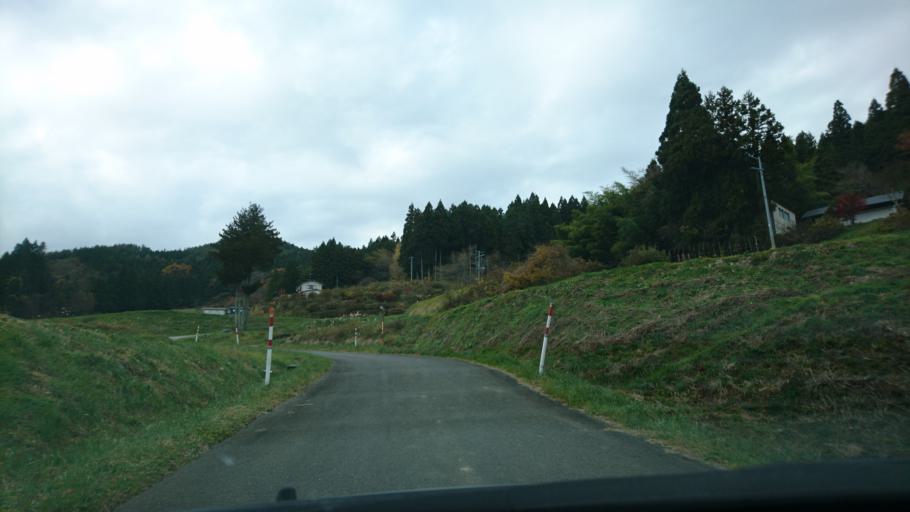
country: JP
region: Iwate
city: Ichinoseki
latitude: 39.0054
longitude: 141.2084
